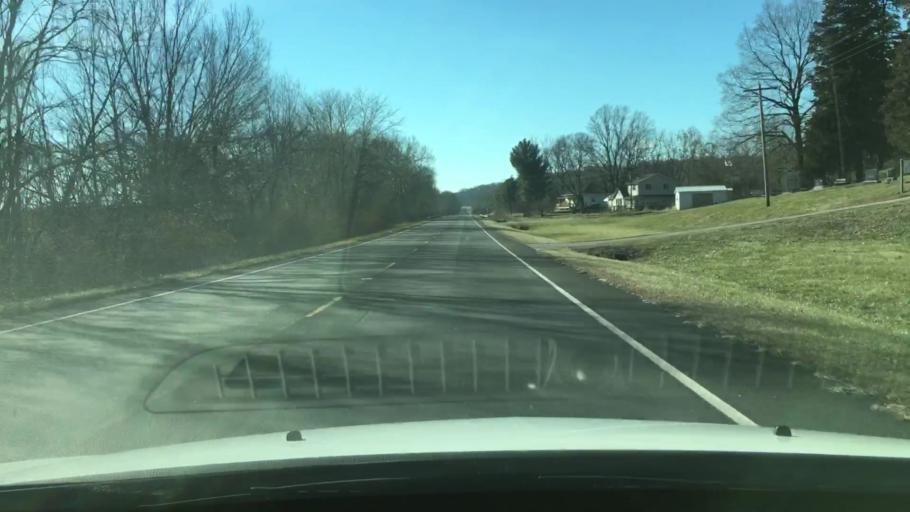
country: US
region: Illinois
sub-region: Fulton County
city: Canton
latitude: 40.4974
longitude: -89.9336
